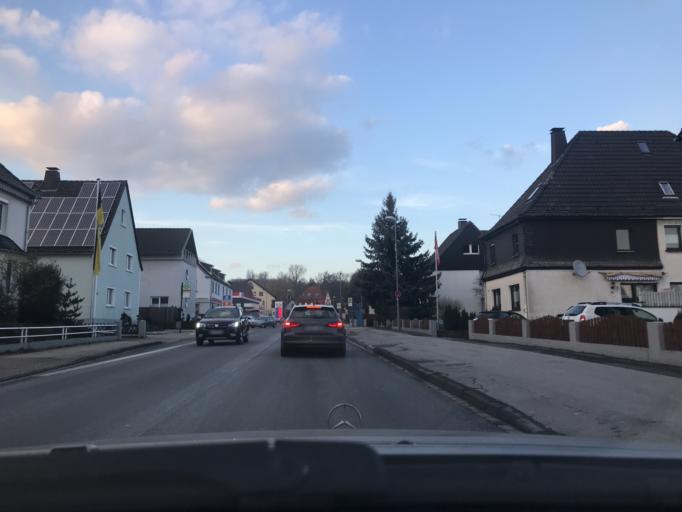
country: DE
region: North Rhine-Westphalia
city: Wickede
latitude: 51.4997
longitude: 7.8704
